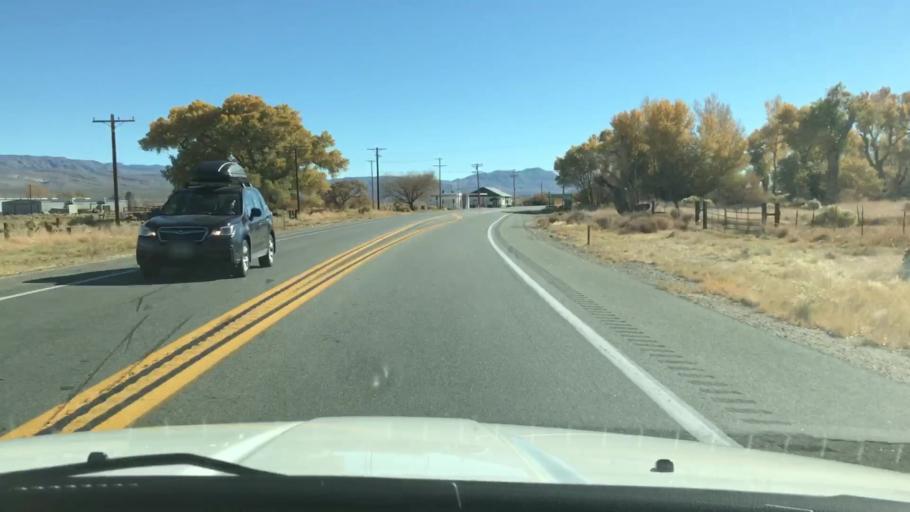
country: US
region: California
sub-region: Inyo County
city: Lone Pine
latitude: 36.2834
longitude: -118.0071
